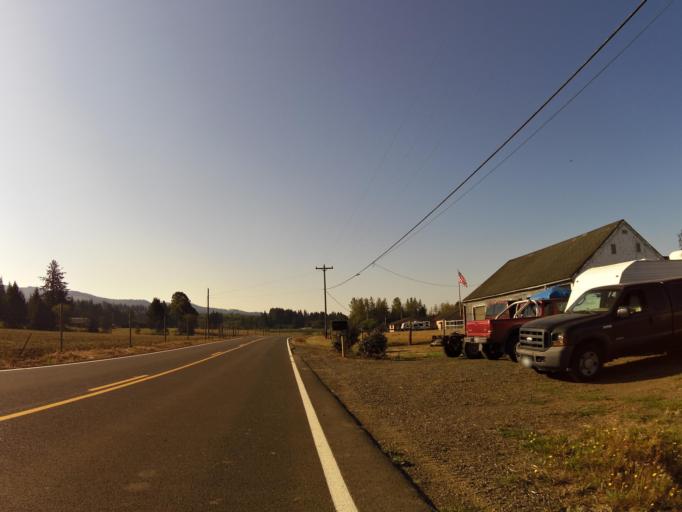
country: US
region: Oregon
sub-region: Tillamook County
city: Tillamook
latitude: 45.3939
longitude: -123.7933
